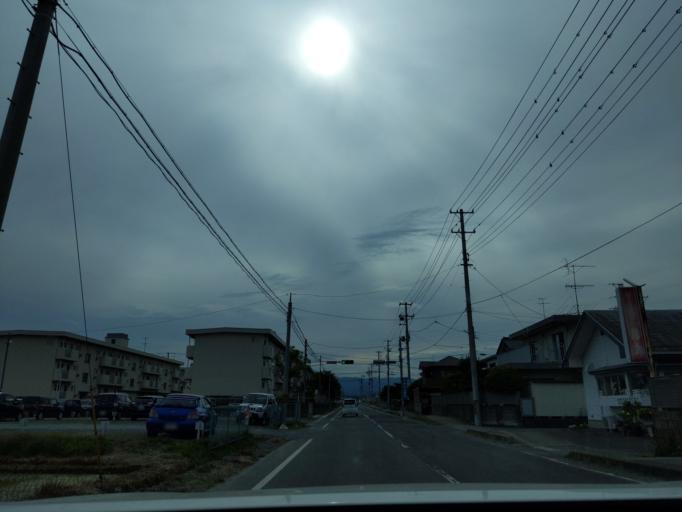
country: JP
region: Fukushima
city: Koriyama
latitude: 37.3738
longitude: 140.3360
